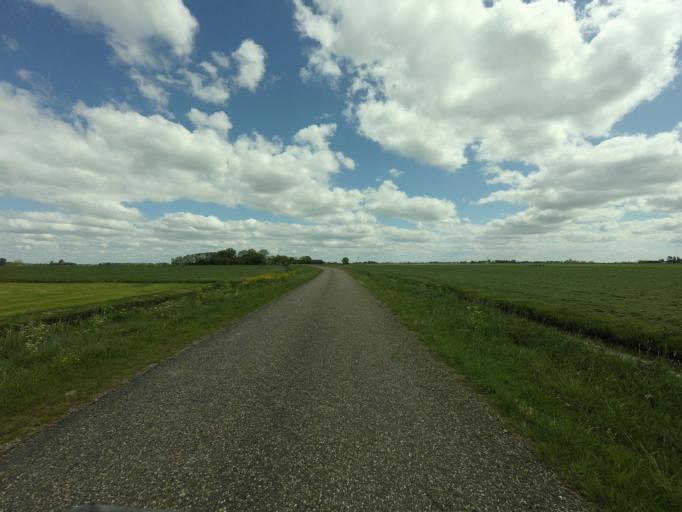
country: NL
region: Friesland
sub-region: Gemeente Franekeradeel
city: Tzum
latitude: 53.1359
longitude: 5.5595
